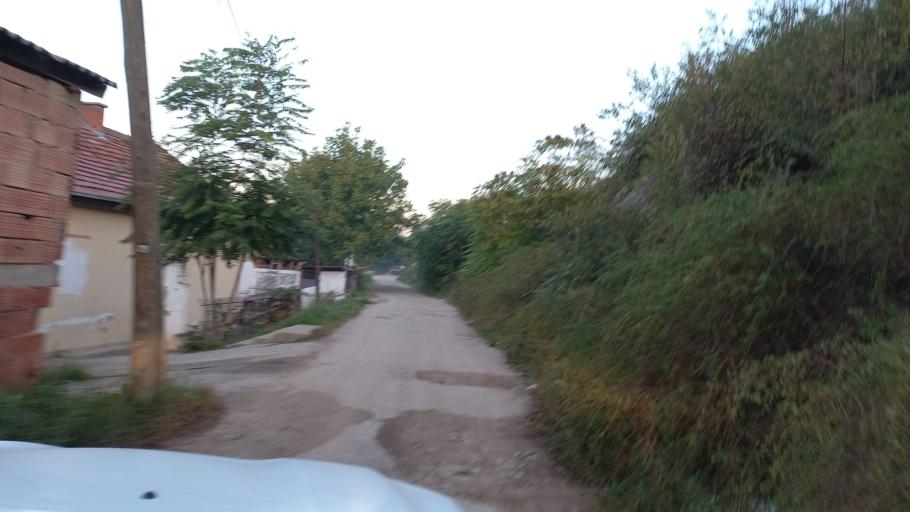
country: MK
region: Kumanovo
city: Kumanovo
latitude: 42.1372
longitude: 21.7290
